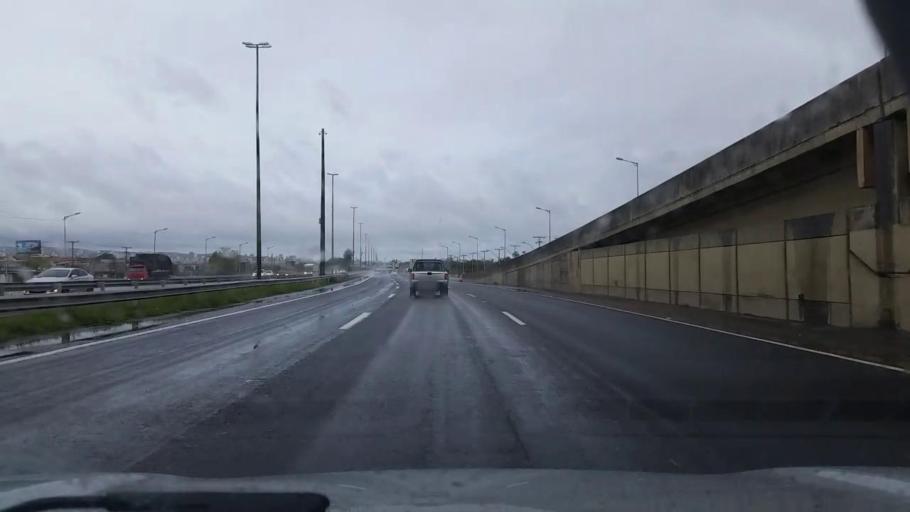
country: BR
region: Rio Grande do Sul
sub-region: Canoas
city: Canoas
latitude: -29.9761
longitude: -51.1997
